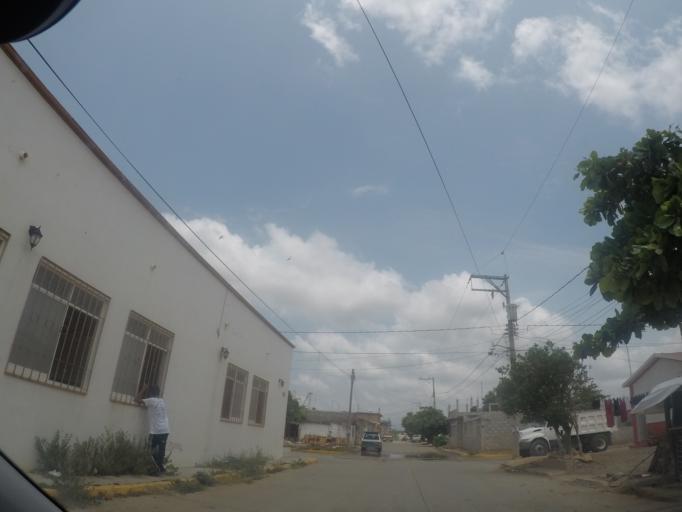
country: MX
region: Oaxaca
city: El Espinal
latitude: 16.5553
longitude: -94.9462
